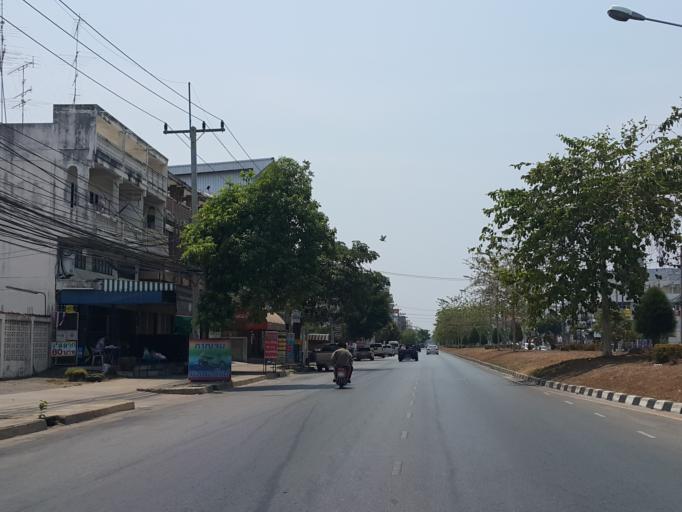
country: TH
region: Kanchanaburi
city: Kanchanaburi
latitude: 14.0397
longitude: 99.5171
